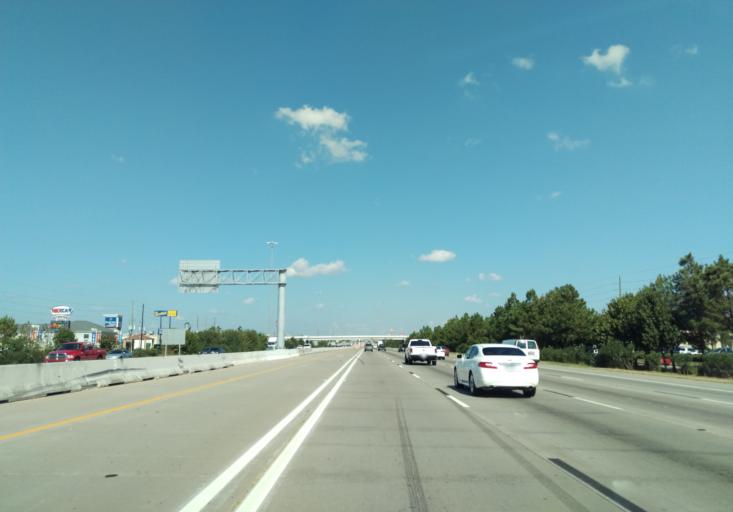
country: US
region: Texas
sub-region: Harris County
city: Spring
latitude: 30.0629
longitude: -95.4337
